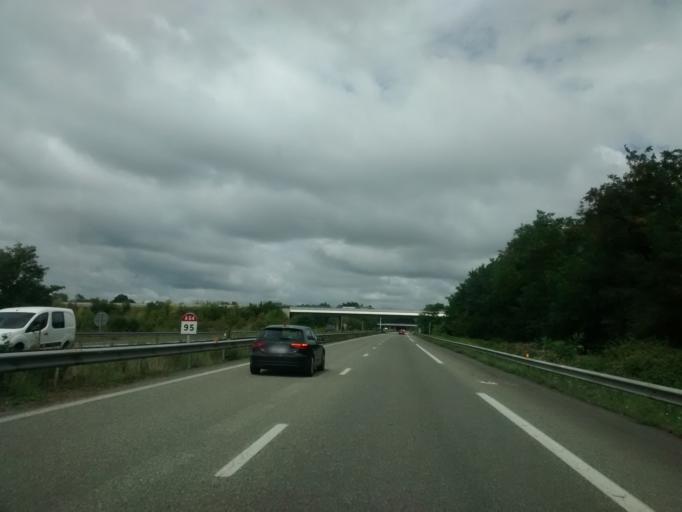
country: FR
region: Aquitaine
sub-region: Departement des Pyrenees-Atlantiques
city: Poey-de-Lescar
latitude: 43.3532
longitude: -0.4461
